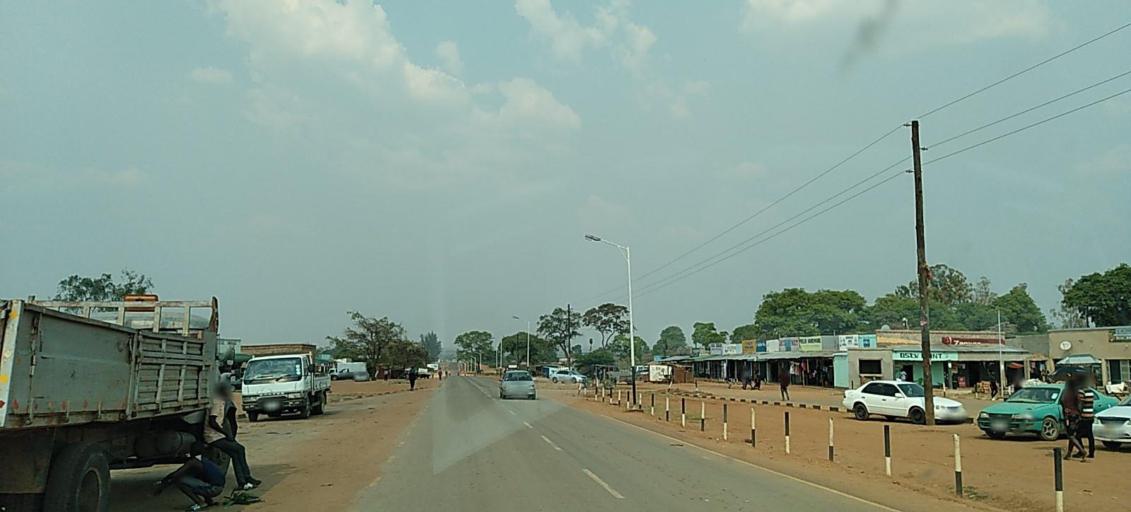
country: ZM
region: North-Western
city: Kabompo
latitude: -13.5937
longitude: 24.2009
